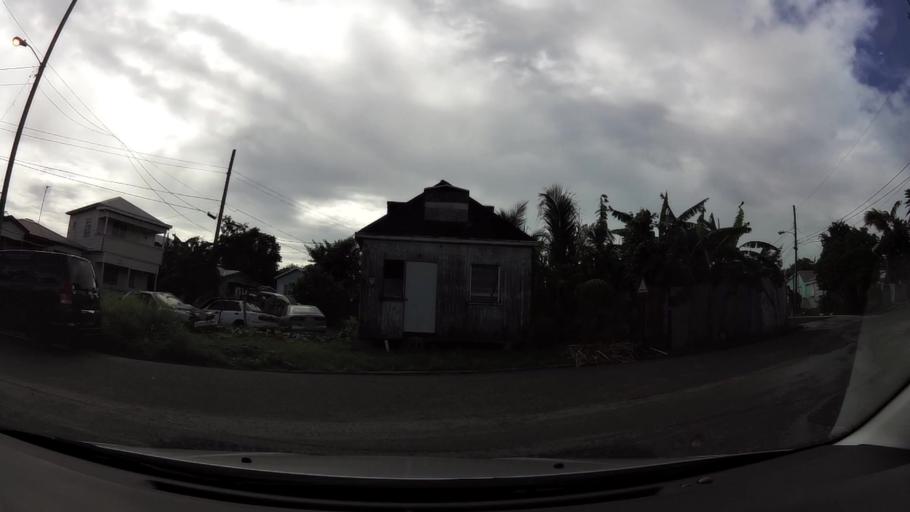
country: AG
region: Saint George
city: Piggotts
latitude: 17.1098
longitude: -61.8166
